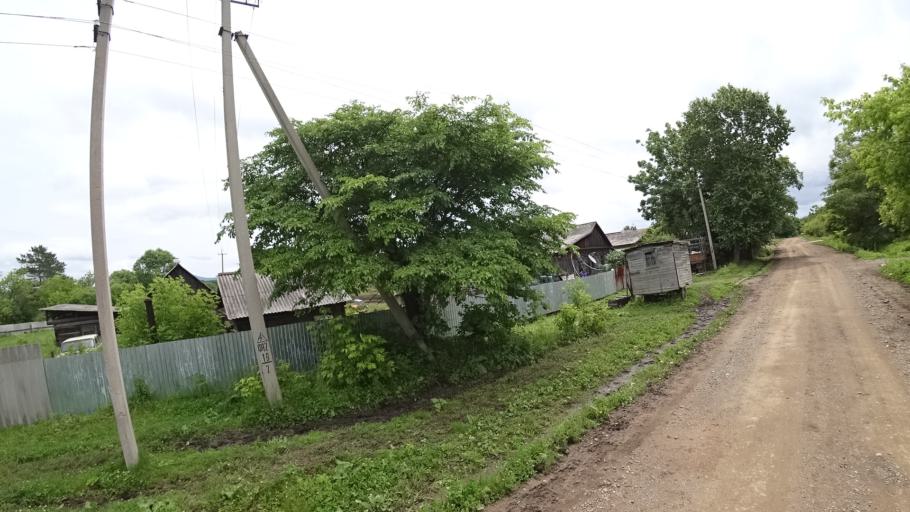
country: RU
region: Primorskiy
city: Novosysoyevka
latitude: 44.2277
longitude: 133.3731
